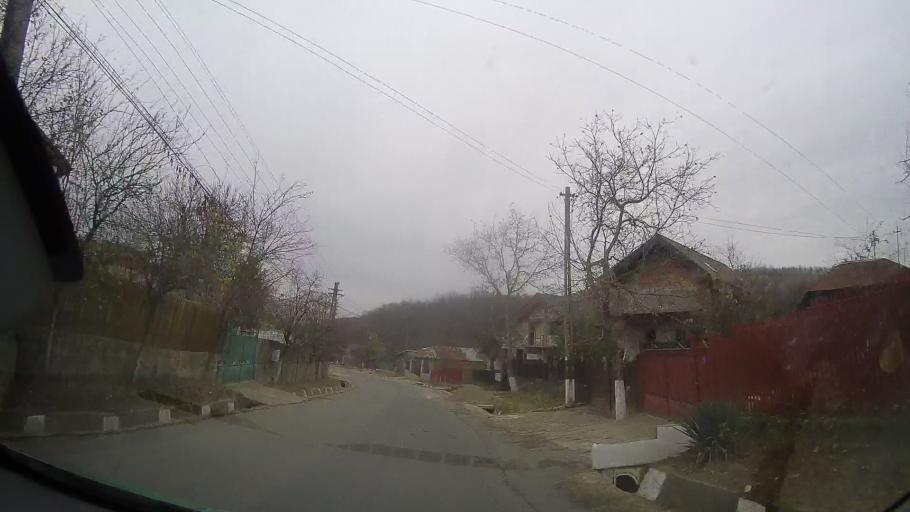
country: RO
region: Prahova
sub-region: Comuna Gornet-Cricov
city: Gornet-Cricov
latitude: 45.0578
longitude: 26.2846
